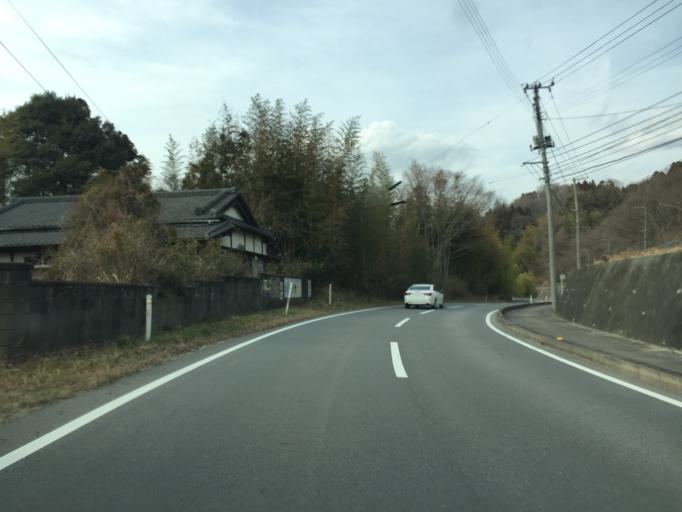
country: JP
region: Fukushima
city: Iwaki
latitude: 36.9962
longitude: 140.7313
